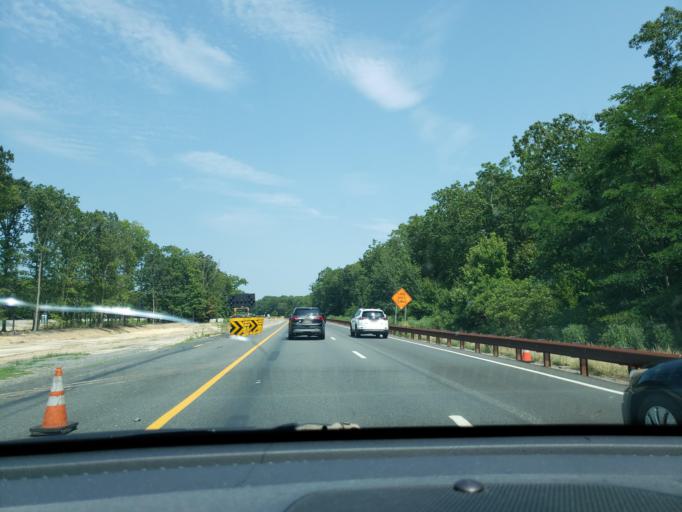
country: US
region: New Jersey
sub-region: Atlantic County
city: Linwood
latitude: 39.3577
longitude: -74.5911
